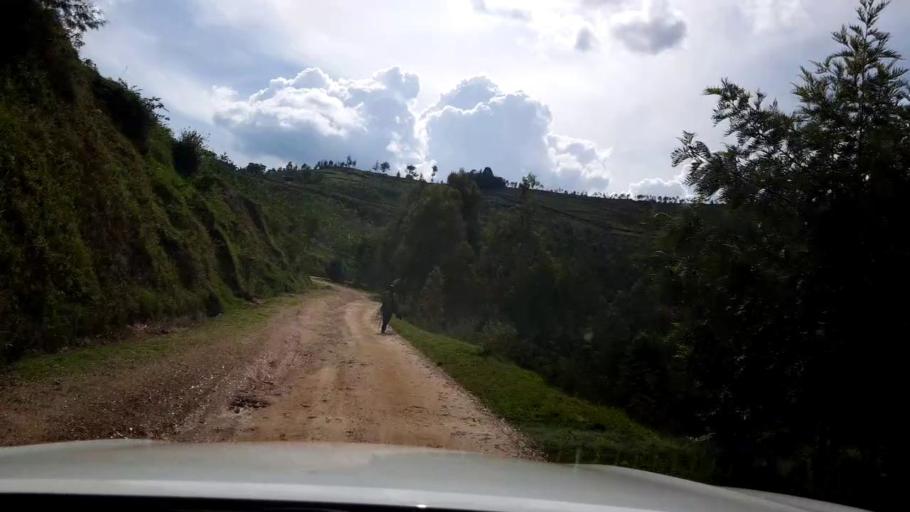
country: RW
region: Southern Province
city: Gitarama
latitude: -1.9947
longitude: 29.7107
